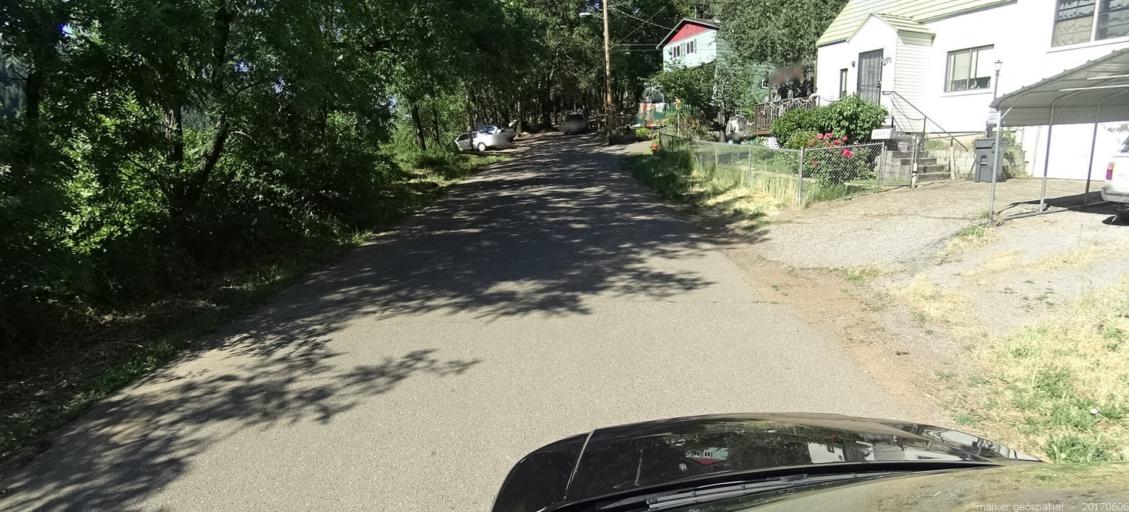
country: US
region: California
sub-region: Siskiyou County
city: Dunsmuir
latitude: 41.2041
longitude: -122.2729
